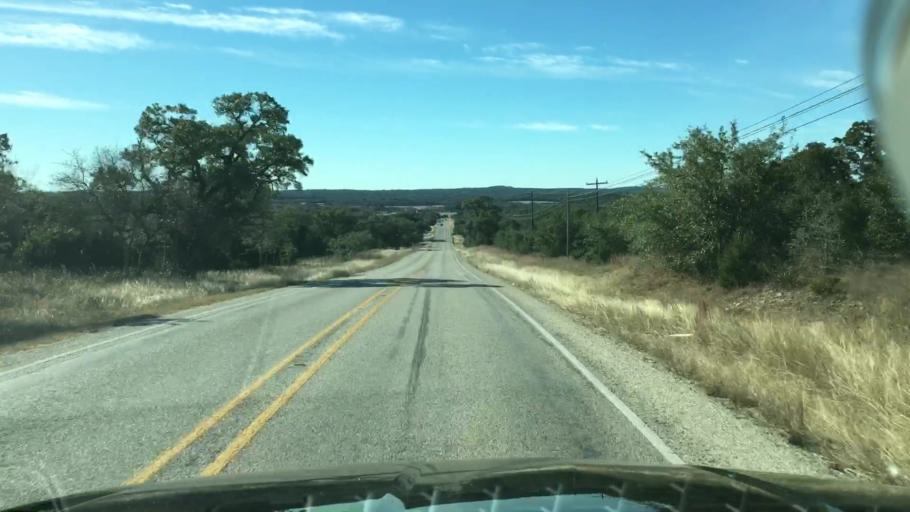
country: US
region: Texas
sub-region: Blanco County
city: Blanco
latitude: 30.1090
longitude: -98.3447
